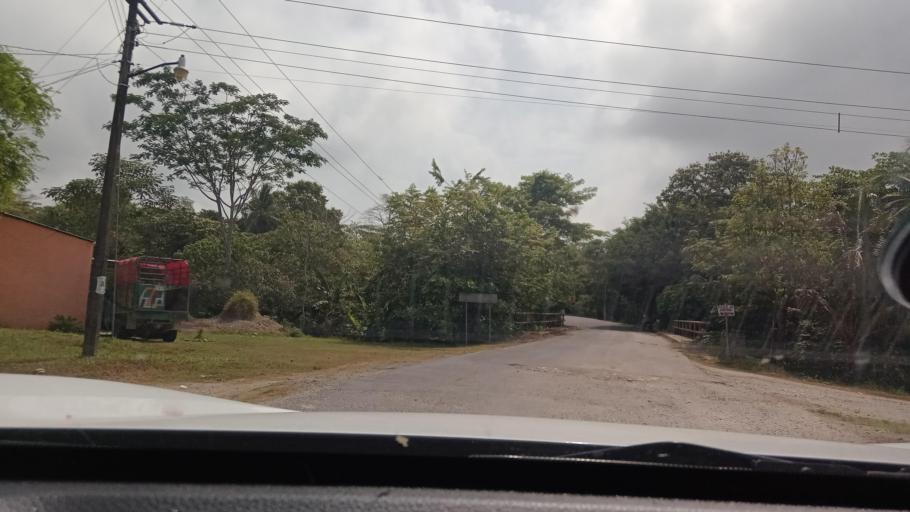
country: MX
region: Tabasco
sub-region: Huimanguillo
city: Francisco Rueda
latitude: 17.5789
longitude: -94.0973
